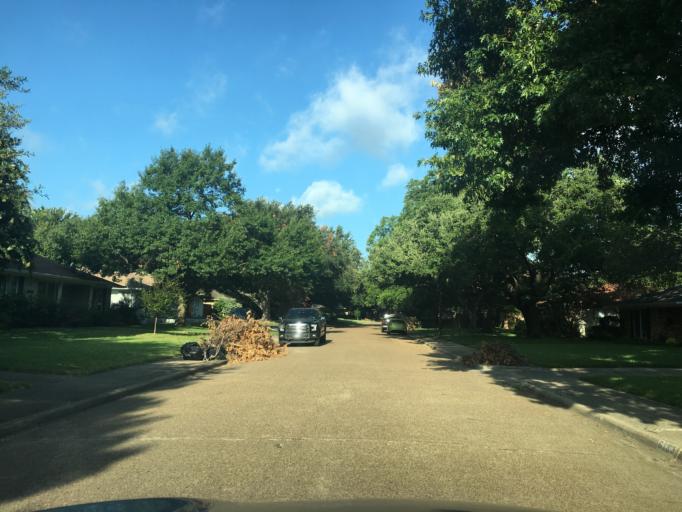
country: US
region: Texas
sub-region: Dallas County
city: Highland Park
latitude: 32.8477
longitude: -96.7591
